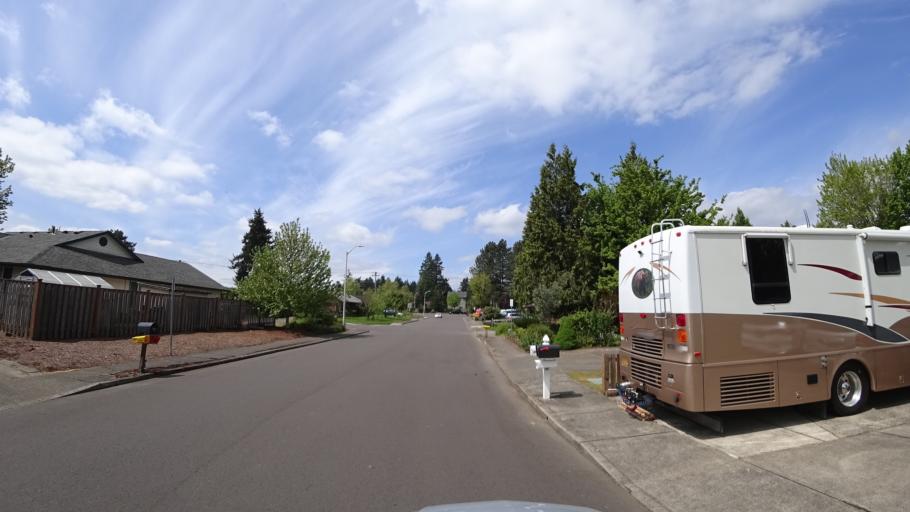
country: US
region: Oregon
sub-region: Washington County
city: Hillsboro
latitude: 45.5383
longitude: -122.9941
